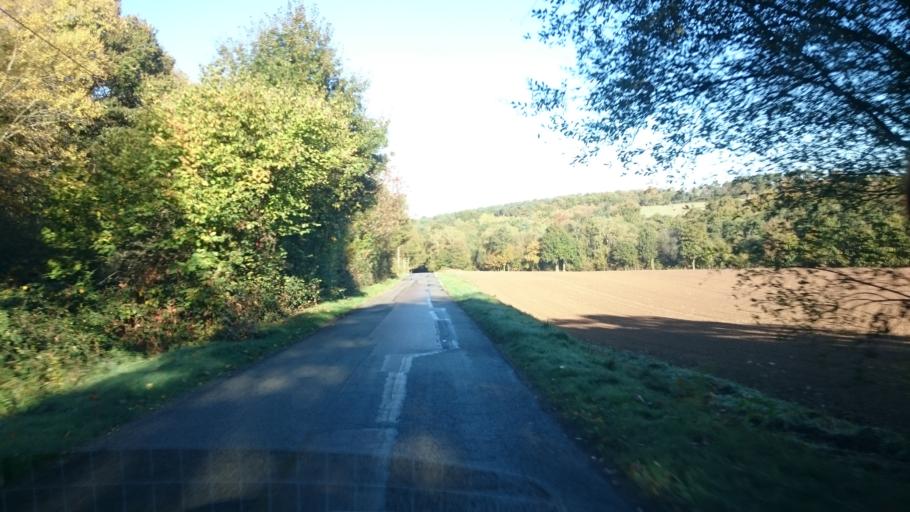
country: FR
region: Brittany
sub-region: Departement d'Ille-et-Vilaine
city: Laille
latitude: 47.9600
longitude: -1.7032
